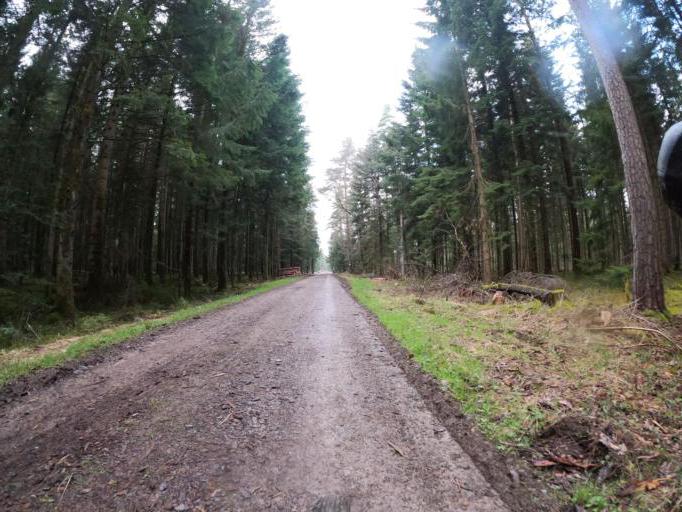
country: DE
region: Baden-Wuerttemberg
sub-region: Karlsruhe Region
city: Oberreichenbach
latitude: 48.7219
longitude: 8.6571
